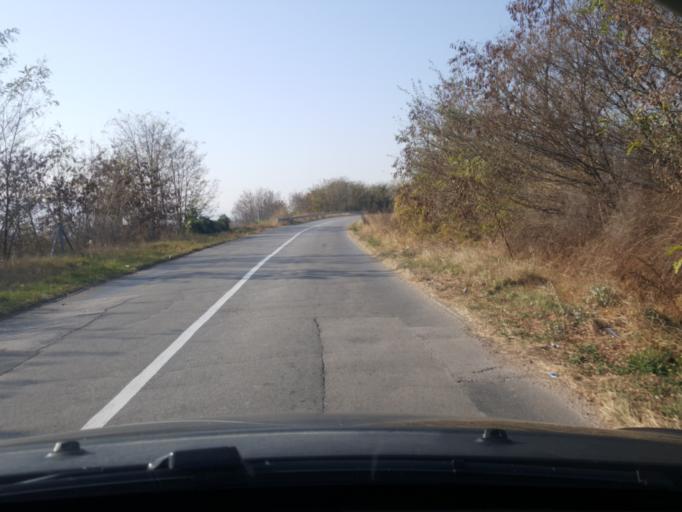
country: RS
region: Central Serbia
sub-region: Nisavski Okrug
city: Niska Banja
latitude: 43.3189
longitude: 22.0064
